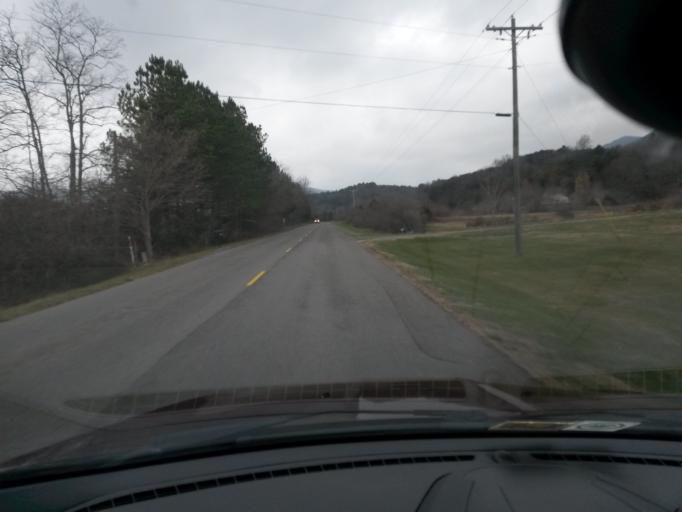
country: US
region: Virginia
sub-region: City of Lexington
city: Lexington
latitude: 37.8627
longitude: -79.5163
